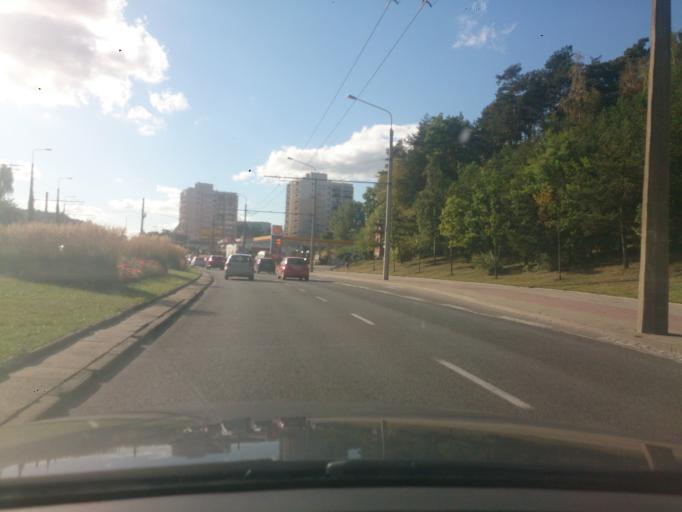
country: PL
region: Pomeranian Voivodeship
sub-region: Gdynia
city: Wielki Kack
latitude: 54.4709
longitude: 18.4931
